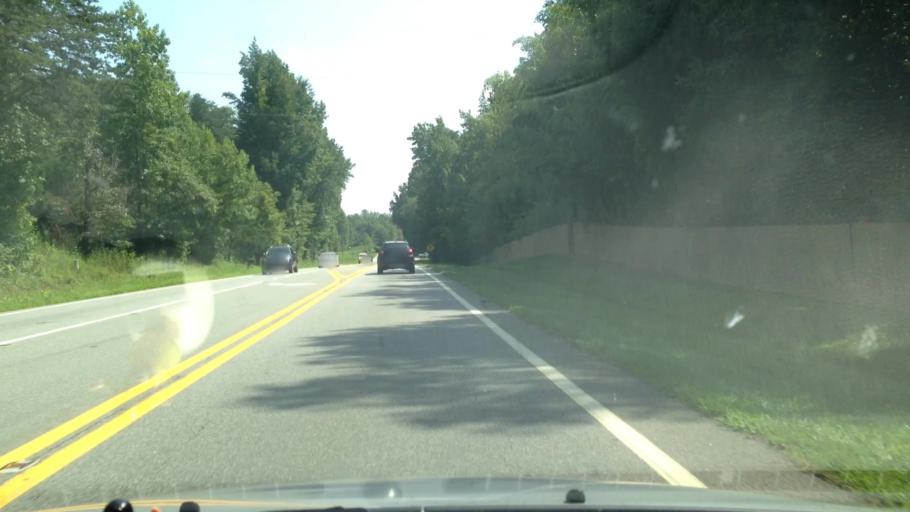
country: US
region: North Carolina
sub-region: Guilford County
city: Oak Ridge
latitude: 36.1898
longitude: -79.9857
